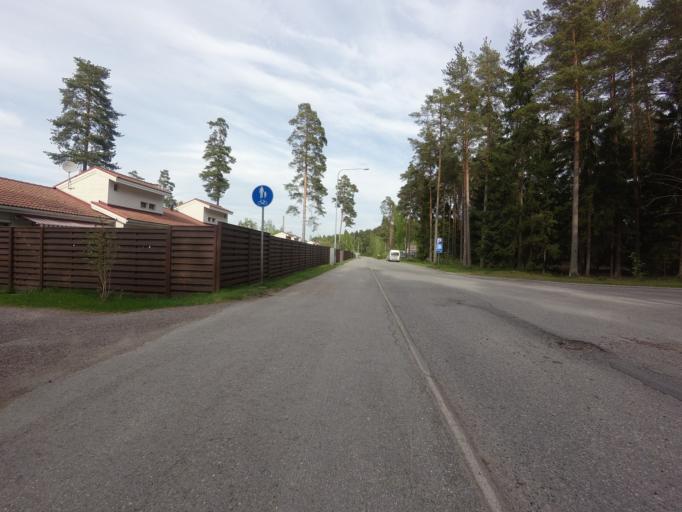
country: FI
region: Uusimaa
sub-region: Helsinki
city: Koukkuniemi
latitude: 60.1448
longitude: 24.6973
